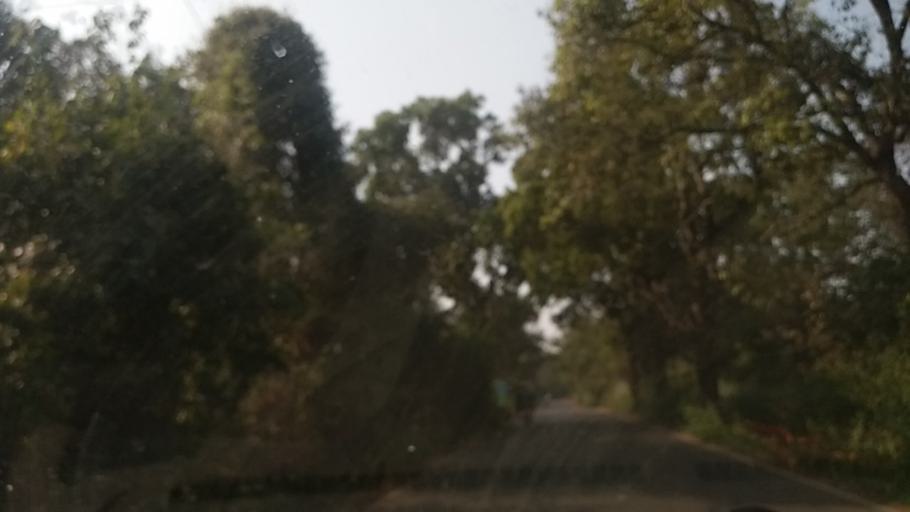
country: IN
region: Goa
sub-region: North Goa
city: Pernem
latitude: 15.7139
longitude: 73.8074
